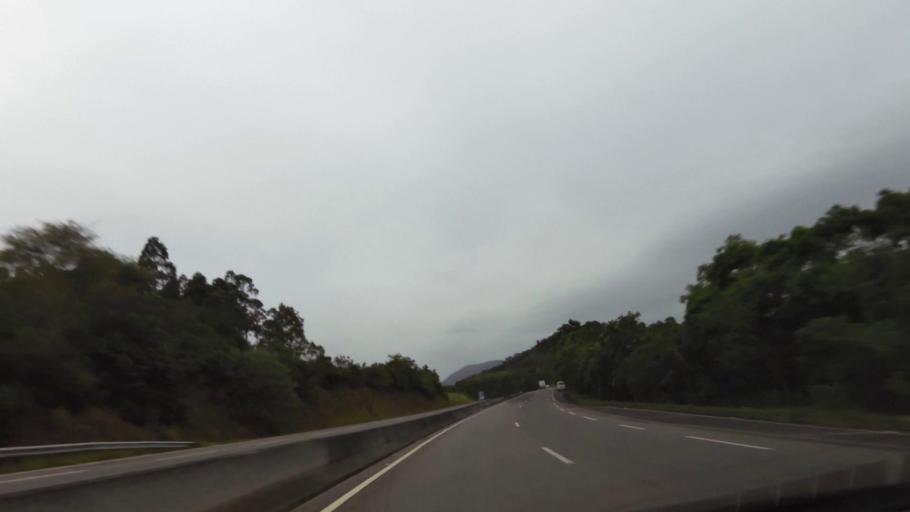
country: BR
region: Espirito Santo
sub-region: Guarapari
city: Guarapari
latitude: -20.6272
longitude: -40.5012
